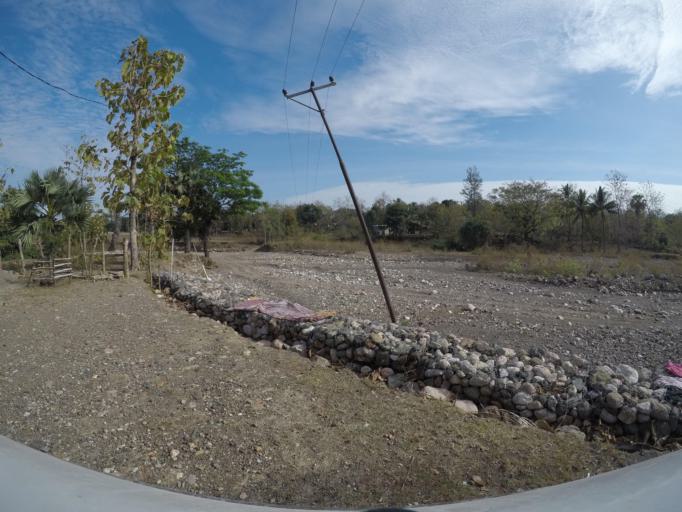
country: TL
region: Bobonaro
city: Maliana
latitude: -8.9933
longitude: 125.2031
